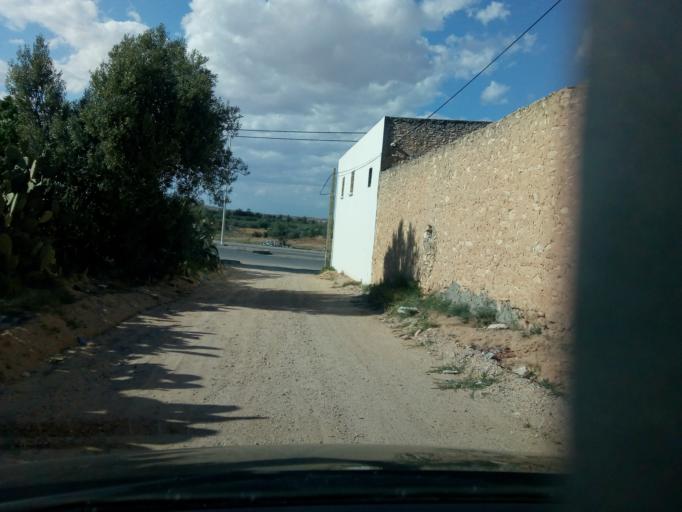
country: TN
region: Safaqis
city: Sfax
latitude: 34.7312
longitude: 10.6019
